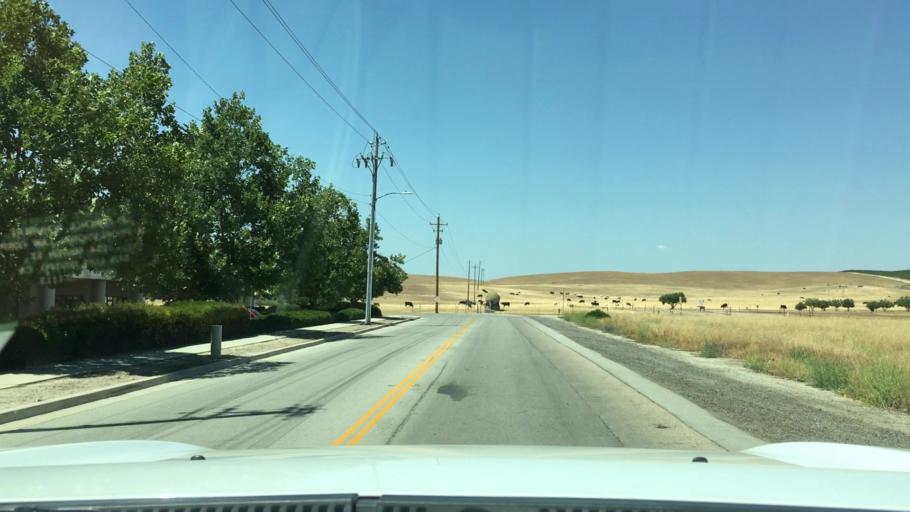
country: US
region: California
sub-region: San Luis Obispo County
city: Paso Robles
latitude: 35.6124
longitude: -120.6443
